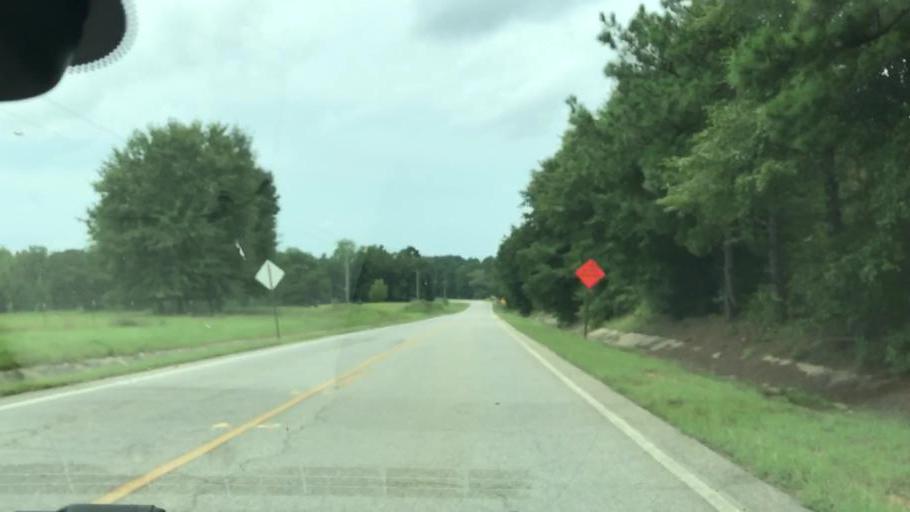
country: US
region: Georgia
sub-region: Clay County
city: Fort Gaines
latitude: 31.6981
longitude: -85.0439
